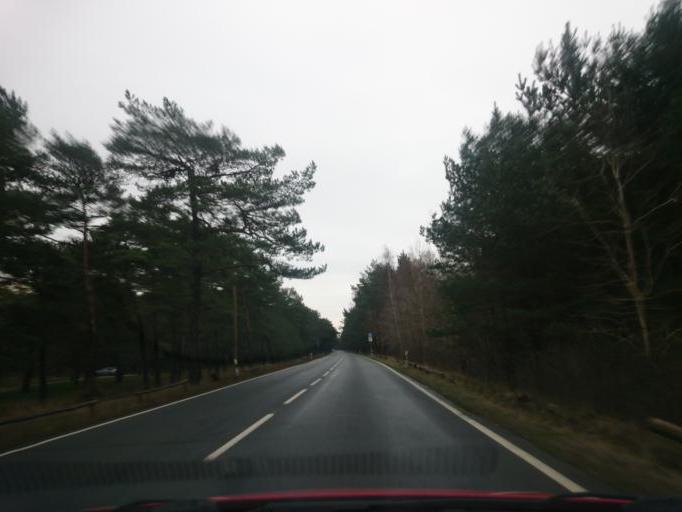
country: DE
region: Mecklenburg-Vorpommern
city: Glowe
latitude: 54.5860
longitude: 13.4013
